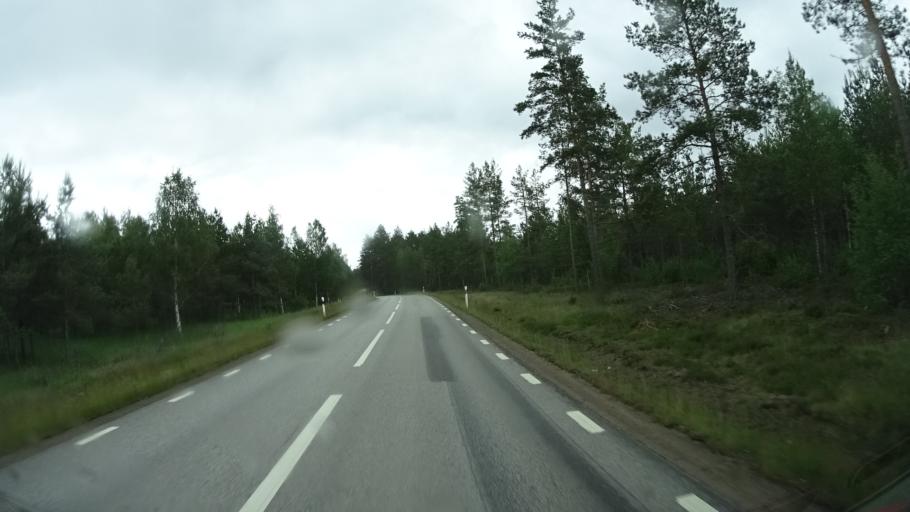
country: SE
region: Kalmar
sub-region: Hultsfreds Kommun
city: Hultsfred
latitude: 57.5320
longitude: 15.7739
